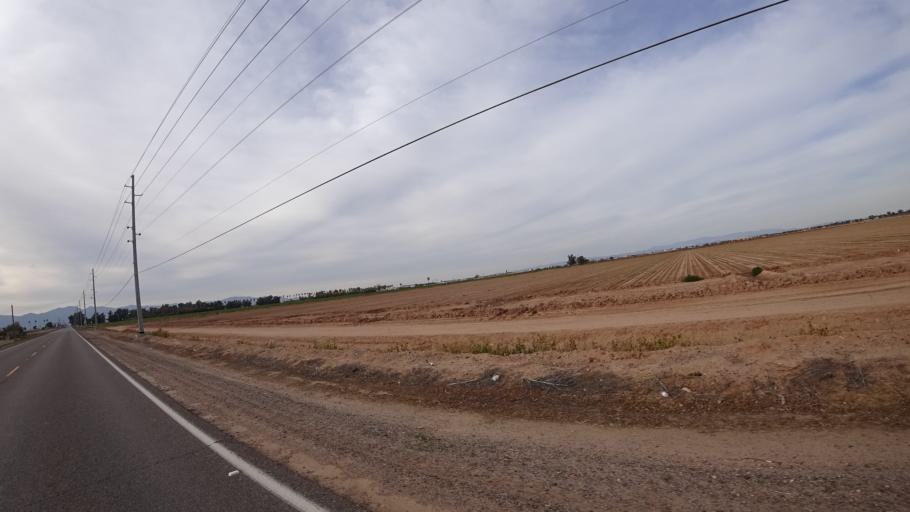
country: US
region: Arizona
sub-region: Maricopa County
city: El Mirage
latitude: 33.5657
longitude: -112.3485
